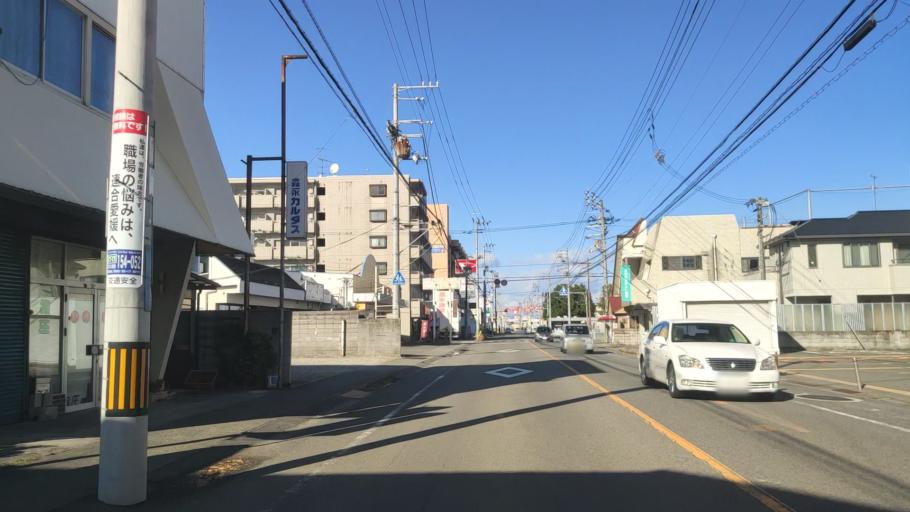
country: JP
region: Ehime
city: Saijo
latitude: 33.9155
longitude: 133.1920
